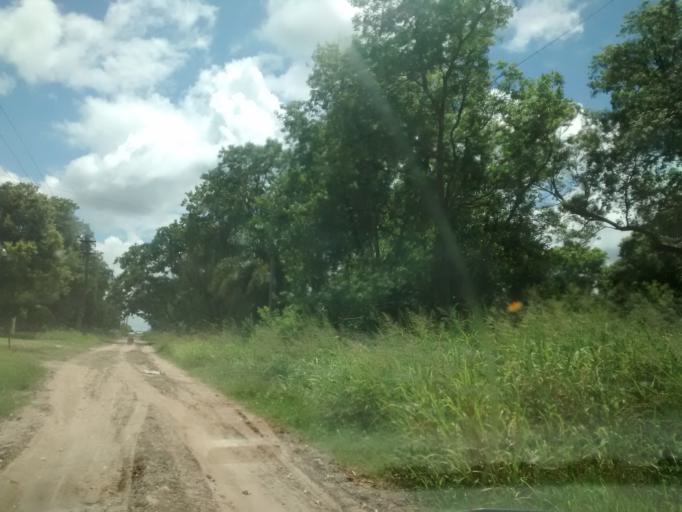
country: AR
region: Chaco
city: Fontana
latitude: -27.4117
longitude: -58.9858
